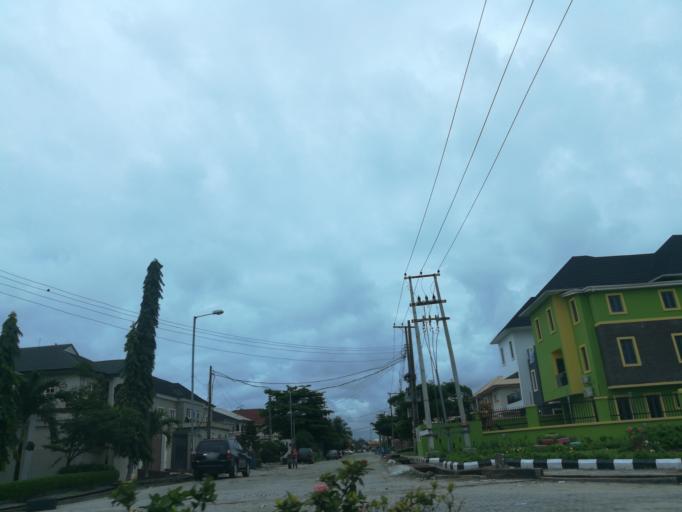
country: NG
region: Lagos
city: Ikoyi
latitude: 6.4317
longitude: 3.4623
